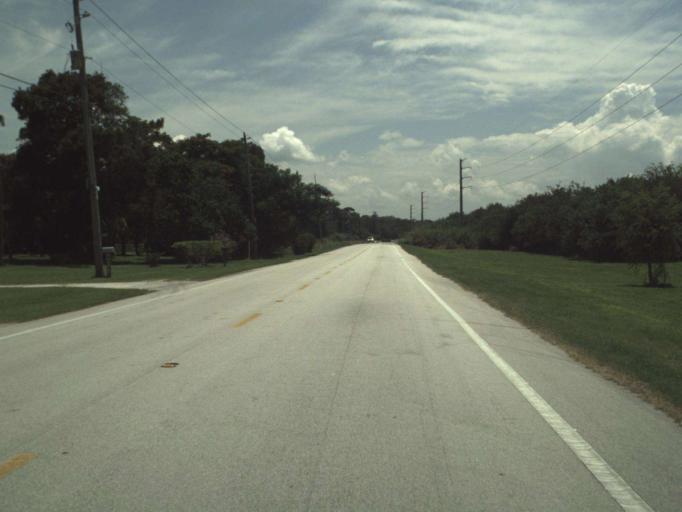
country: US
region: Florida
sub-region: Palm Beach County
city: Pahokee
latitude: 26.8985
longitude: -80.6115
